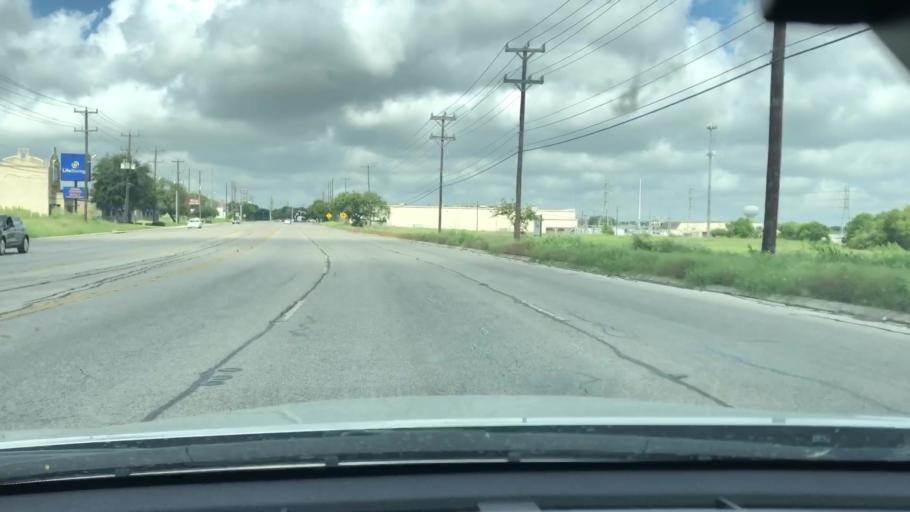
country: US
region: Texas
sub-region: Bexar County
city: Windcrest
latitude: 29.5062
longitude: -98.3682
